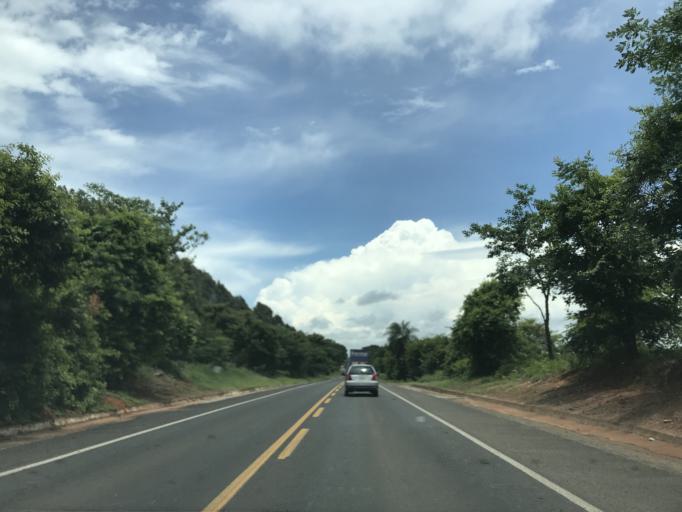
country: BR
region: Minas Gerais
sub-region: Frutal
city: Frutal
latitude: -19.6936
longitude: -48.9838
